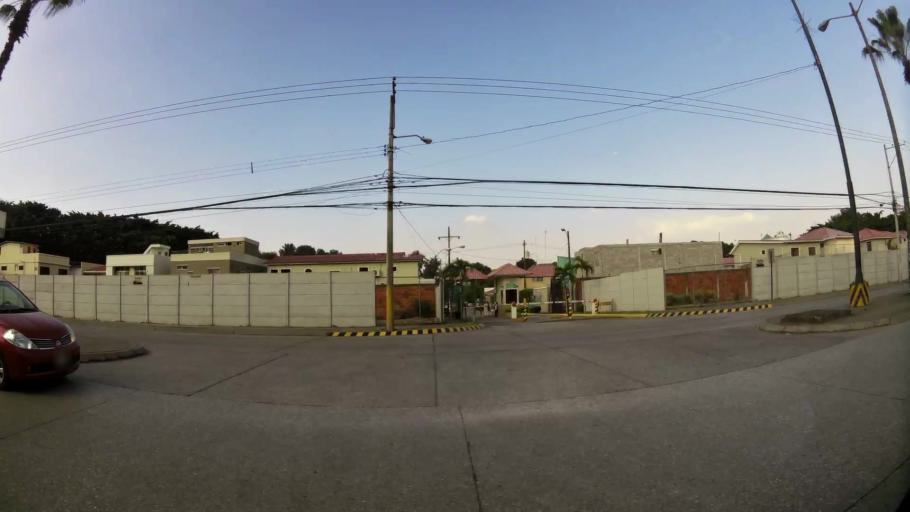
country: EC
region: Guayas
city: Guayaquil
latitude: -2.1519
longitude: -79.9053
